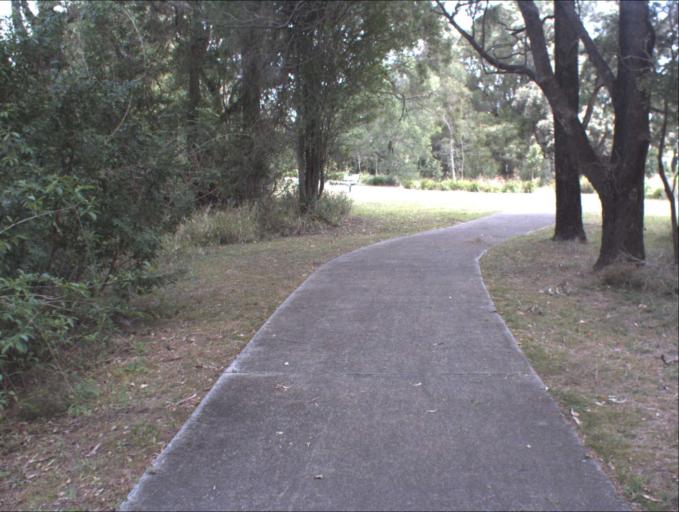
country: AU
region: Queensland
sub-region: Logan
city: Slacks Creek
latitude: -27.6687
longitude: 153.1593
